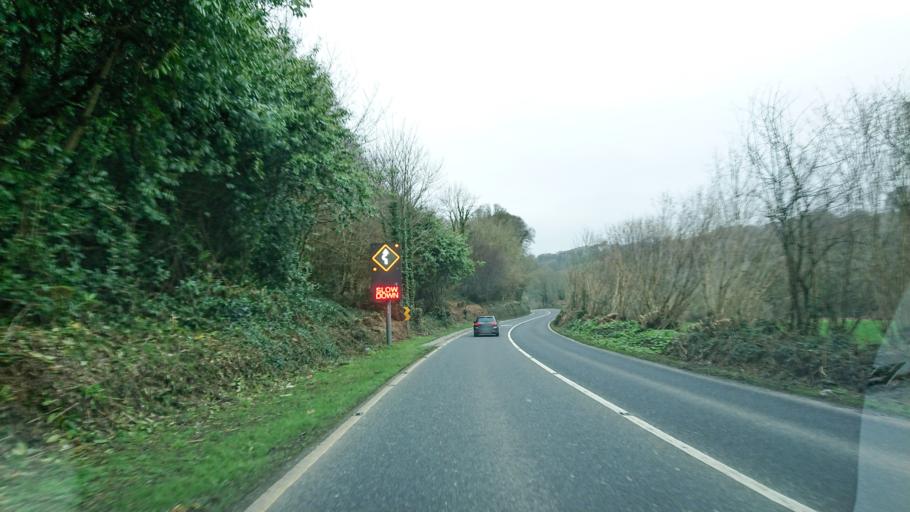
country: IE
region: Munster
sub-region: County Cork
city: Bandon
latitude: 51.7653
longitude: -8.6692
